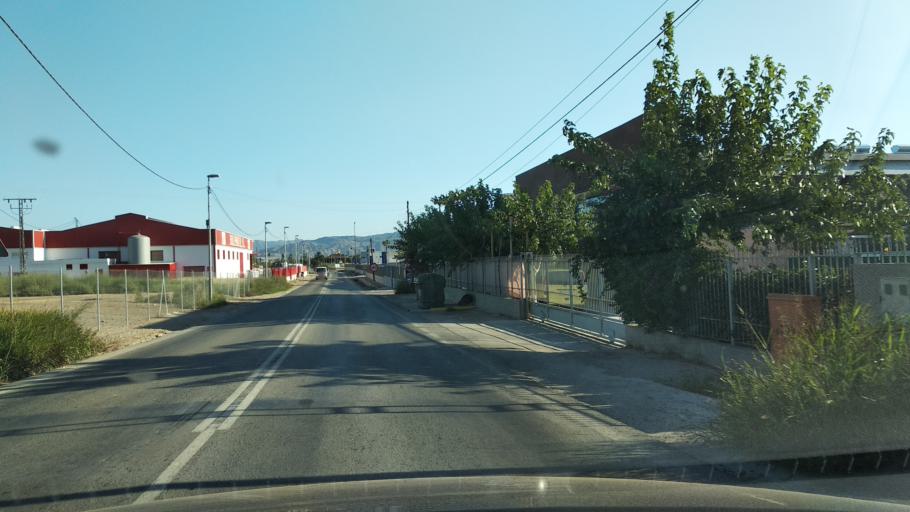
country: ES
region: Murcia
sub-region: Murcia
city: Santomera
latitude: 38.0517
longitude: -1.0564
